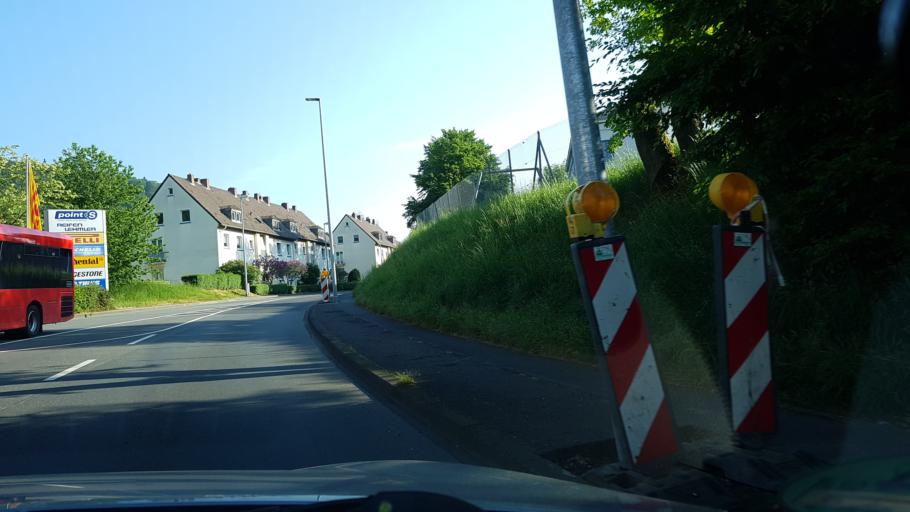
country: DE
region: Rheinland-Pfalz
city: Bad Ems
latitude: 50.3476
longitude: 7.7196
